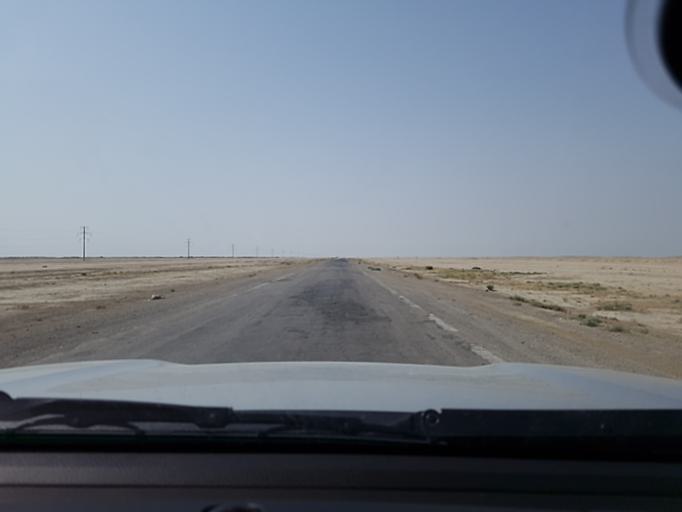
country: TM
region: Balkan
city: Gumdag
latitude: 38.8482
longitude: 54.5954
